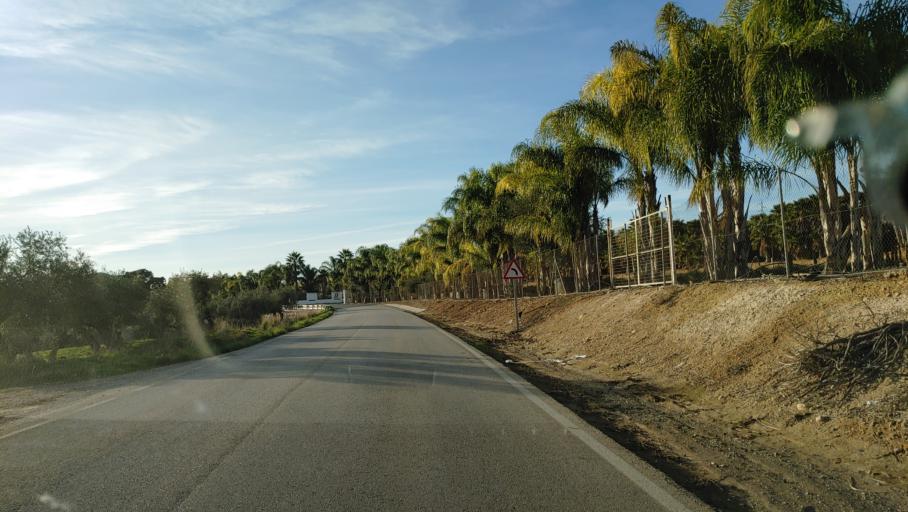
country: ES
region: Andalusia
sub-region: Provincia de Malaga
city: Cartama
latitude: 36.6790
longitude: -4.6233
